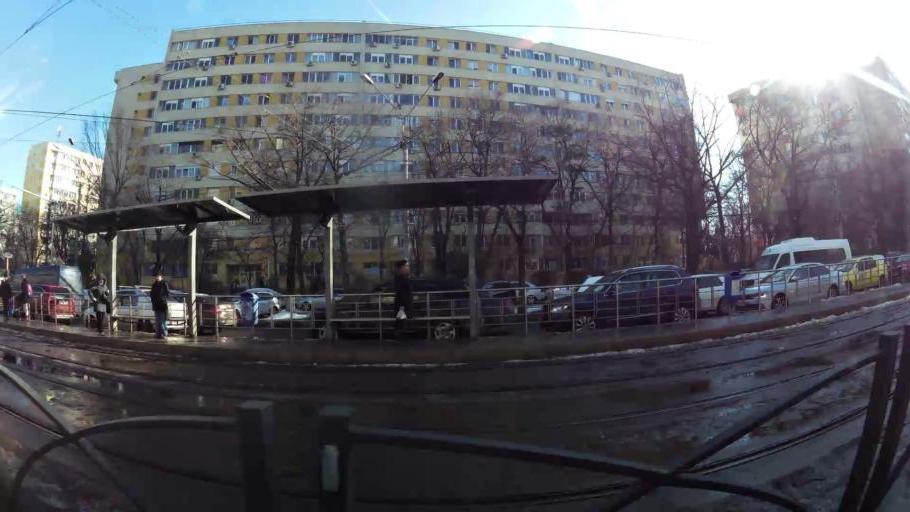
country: RO
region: Bucuresti
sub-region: Municipiul Bucuresti
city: Bucharest
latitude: 44.4564
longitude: 26.1298
